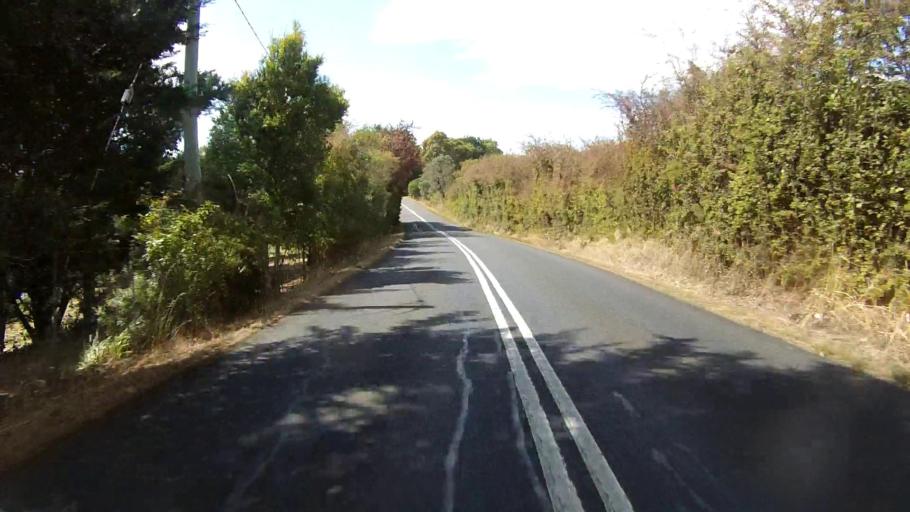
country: AU
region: Tasmania
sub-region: Derwent Valley
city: New Norfolk
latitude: -42.7338
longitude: 146.9127
